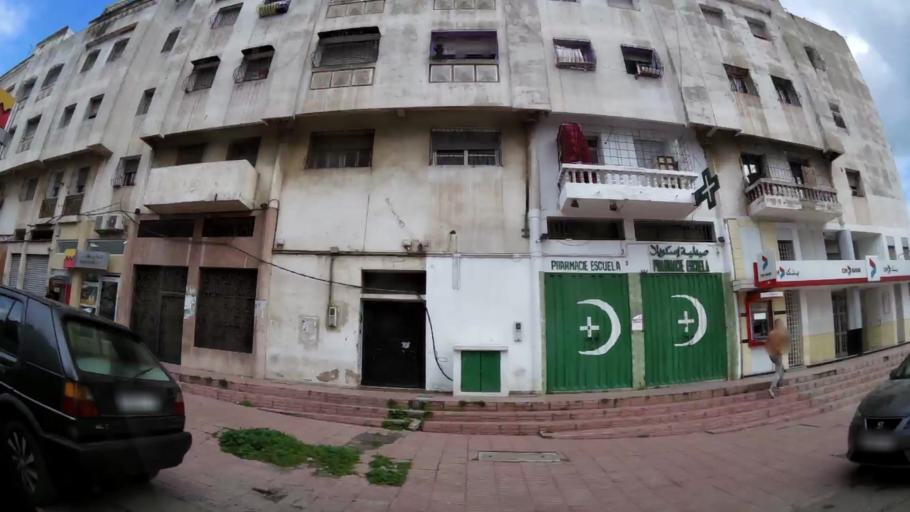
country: MA
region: Grand Casablanca
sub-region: Mediouna
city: Tit Mellil
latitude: 33.5982
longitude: -7.4885
